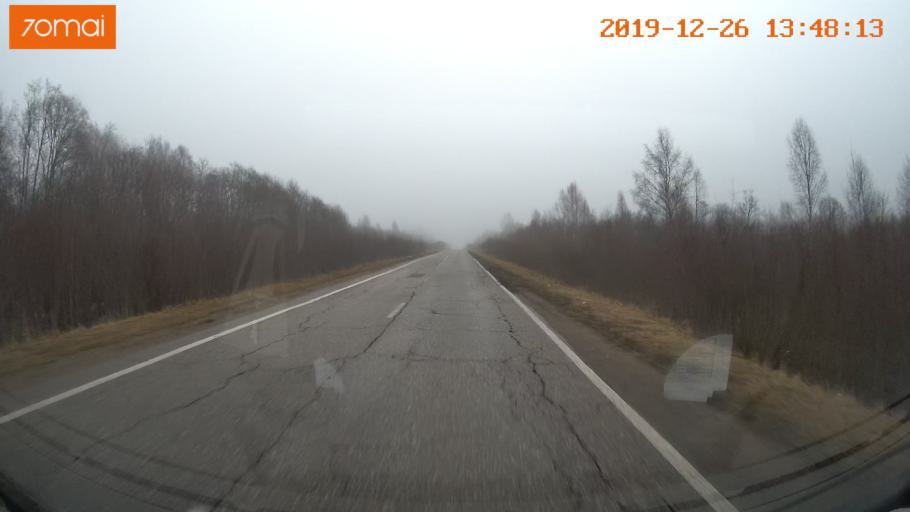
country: RU
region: Vologda
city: Sheksna
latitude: 58.6780
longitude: 38.5447
